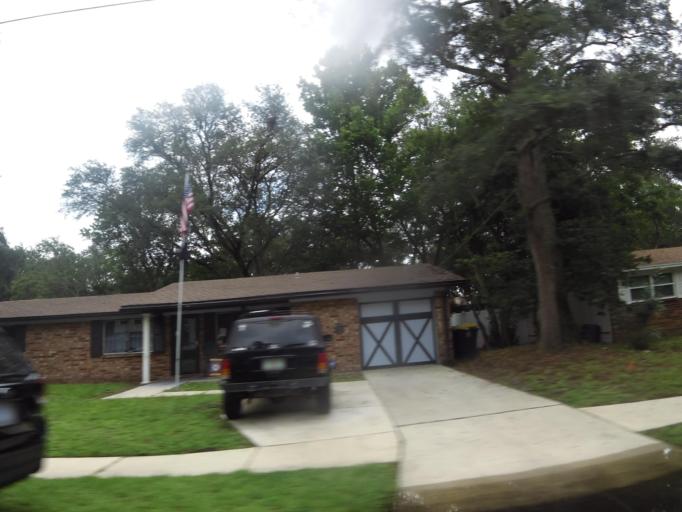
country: US
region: Florida
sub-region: Duval County
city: Jacksonville Beach
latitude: 30.2794
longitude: -81.4338
